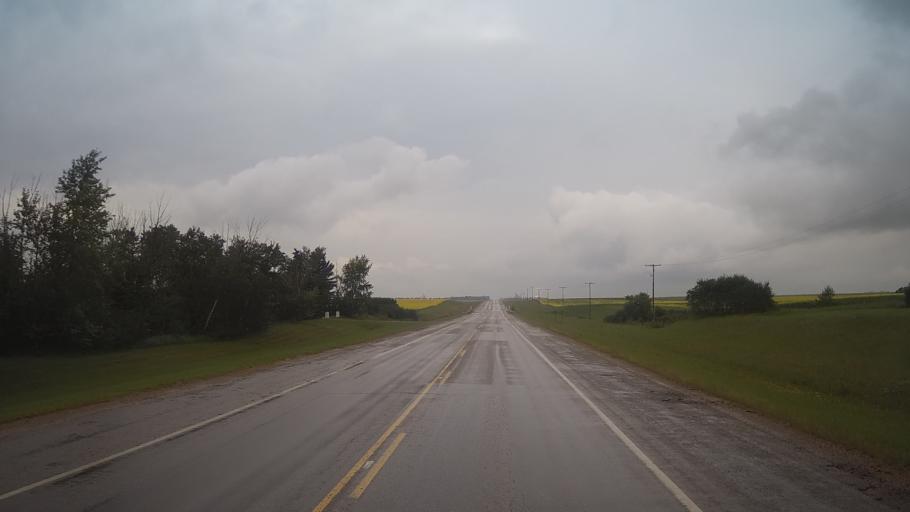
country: CA
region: Saskatchewan
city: Unity
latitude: 52.4350
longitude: -109.0394
